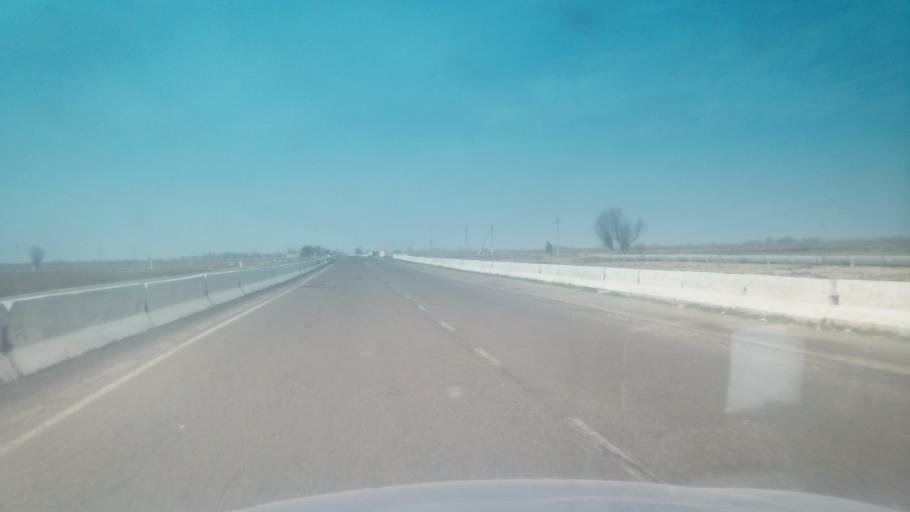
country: KZ
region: Ongtustik Qazaqstan
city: Myrzakent
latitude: 40.5189
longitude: 68.4715
